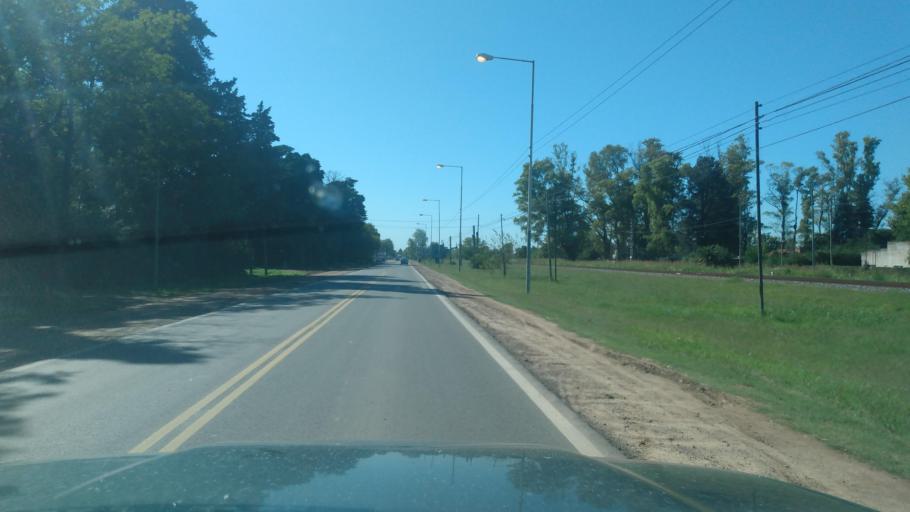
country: AR
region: Buenos Aires
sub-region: Partido de General Rodriguez
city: General Rodriguez
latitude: -34.6047
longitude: -58.9697
